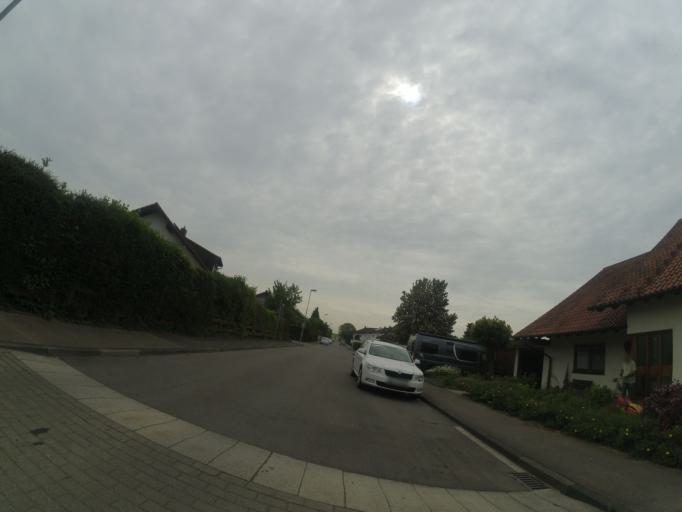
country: DE
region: Baden-Wuerttemberg
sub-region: Tuebingen Region
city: Erbach
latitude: 48.3377
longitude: 9.9404
